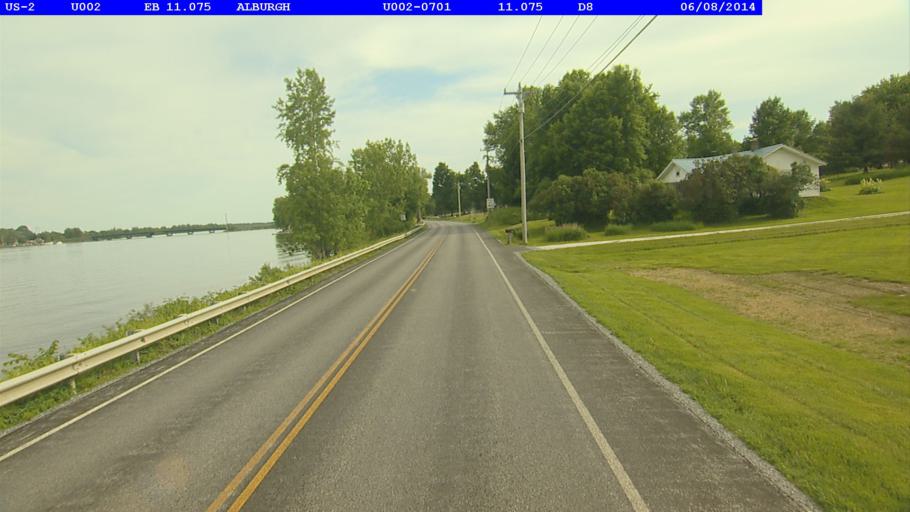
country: US
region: Vermont
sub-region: Grand Isle County
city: North Hero
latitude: 44.8936
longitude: -73.2776
